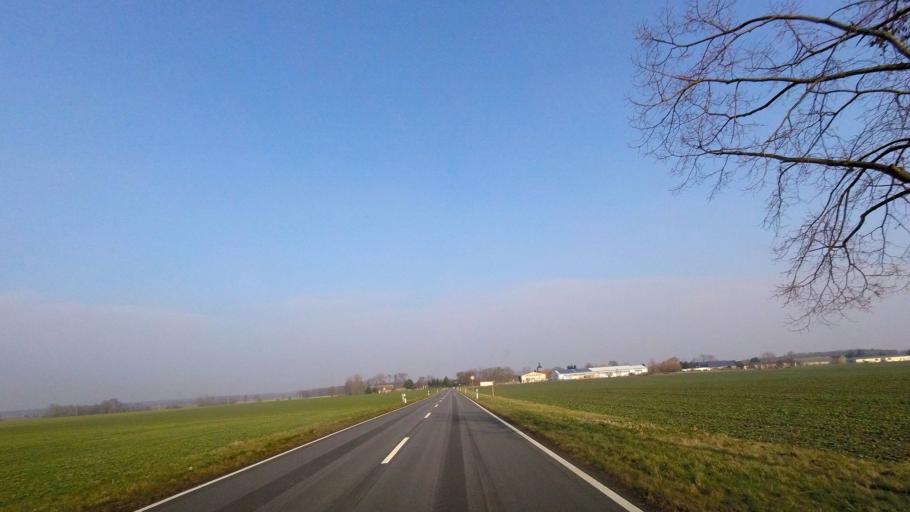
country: DE
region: Brandenburg
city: Juterbog
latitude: 51.9587
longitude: 13.0410
